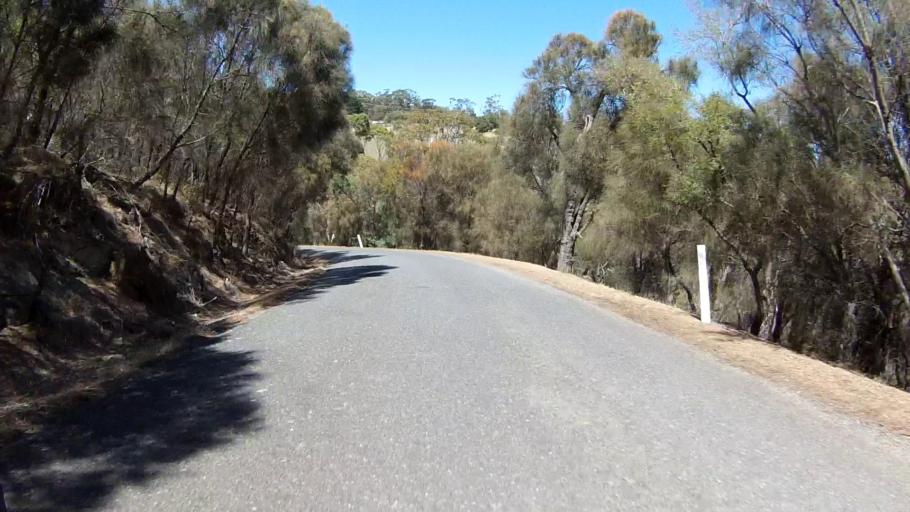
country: AU
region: Tasmania
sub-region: Clarence
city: Cambridge
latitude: -42.8512
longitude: 147.4244
